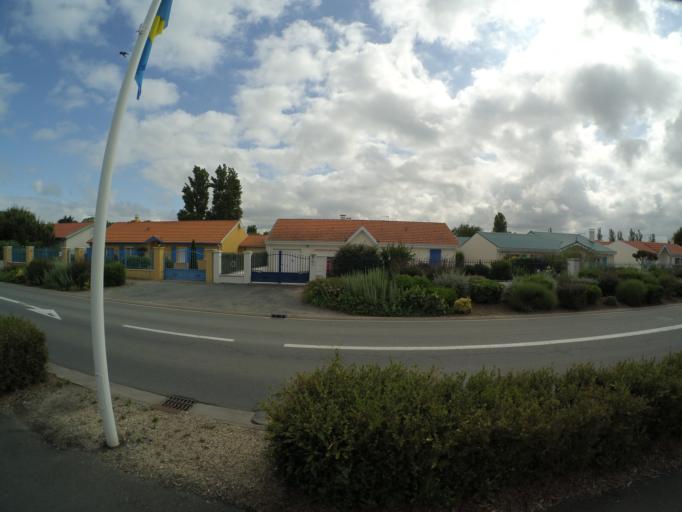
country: FR
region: Poitou-Charentes
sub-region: Departement de la Charente-Maritime
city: Chatelaillon-Plage
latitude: 46.0867
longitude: -1.0954
